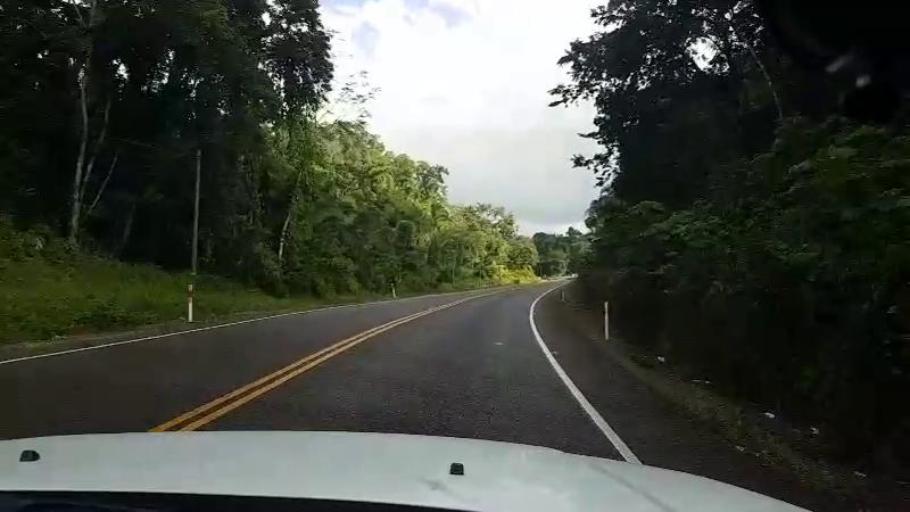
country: BZ
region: Cayo
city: Belmopan
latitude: 17.1498
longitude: -88.7163
